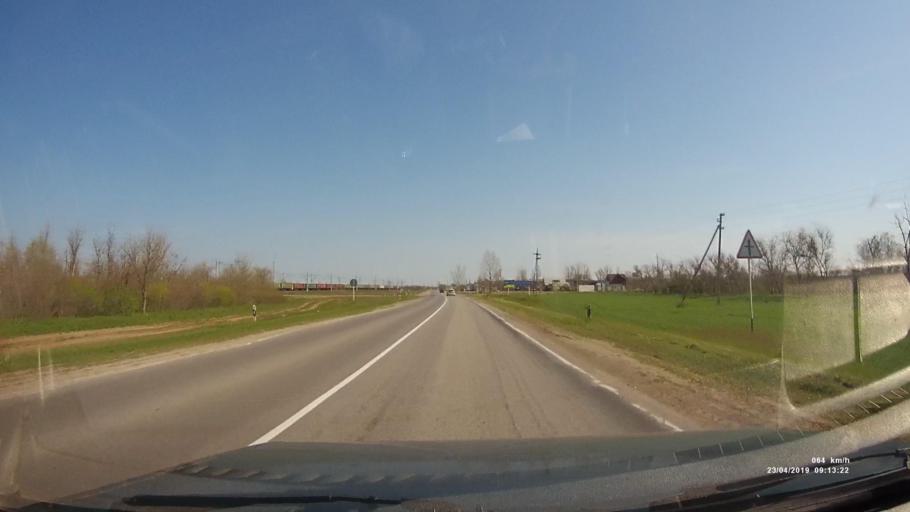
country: RU
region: Rostov
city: Proletarsk
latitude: 46.6156
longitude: 41.6490
